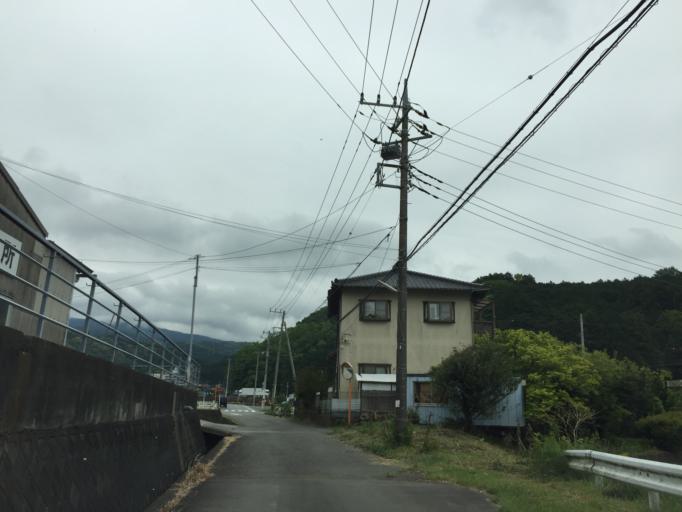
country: JP
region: Shizuoka
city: Mishima
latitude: 35.1769
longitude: 138.9273
